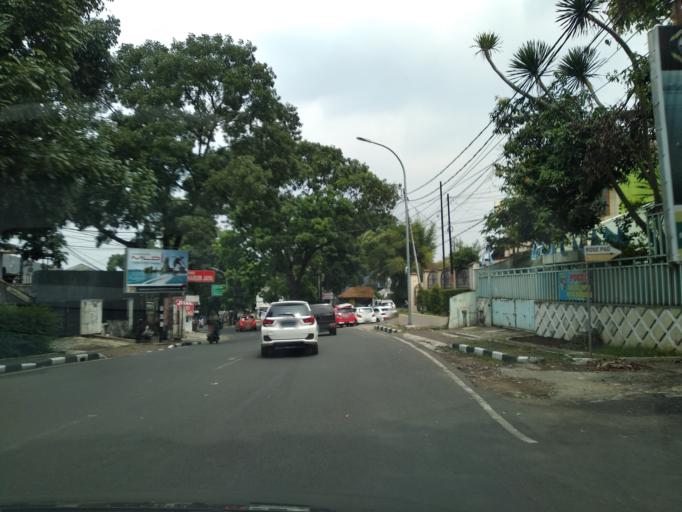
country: ID
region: West Java
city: Bandung
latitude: -6.8768
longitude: 107.5976
